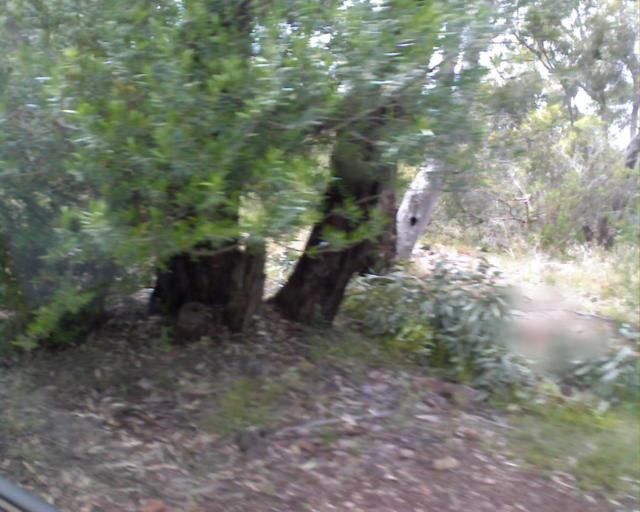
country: AU
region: South Australia
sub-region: Port Pirie City and Dists
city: Port Pirie
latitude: -32.8222
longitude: 138.1855
